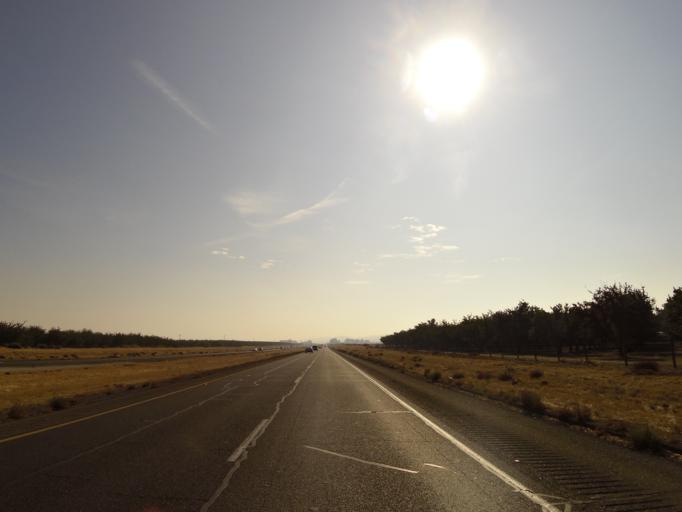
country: US
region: California
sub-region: Kings County
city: Avenal
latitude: 36.1035
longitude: -120.1278
